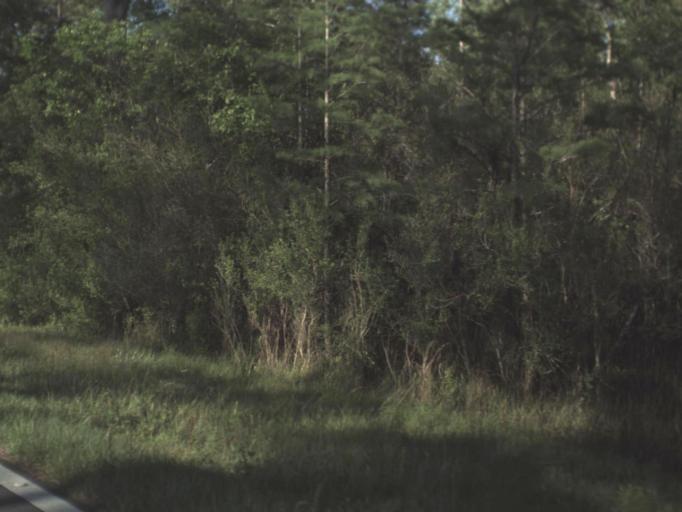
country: US
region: Florida
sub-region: Liberty County
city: Bristol
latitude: 30.3077
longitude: -84.8304
